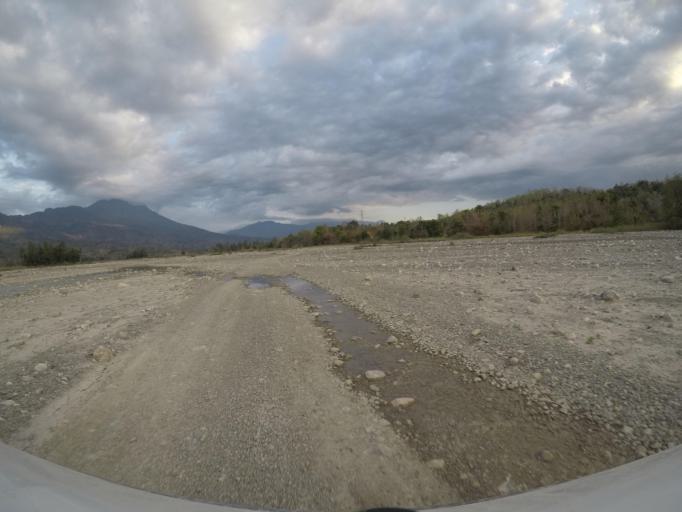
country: TL
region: Bobonaro
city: Maliana
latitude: -8.9065
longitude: 125.2109
